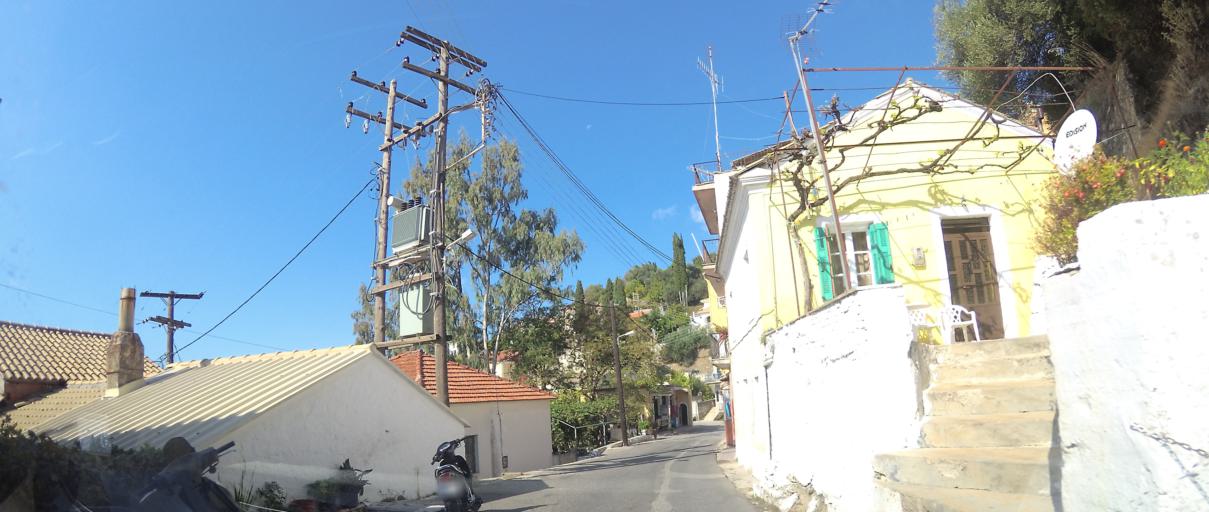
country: GR
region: Ionian Islands
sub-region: Nomos Kerkyras
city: Acharavi
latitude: 39.7214
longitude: 19.8426
